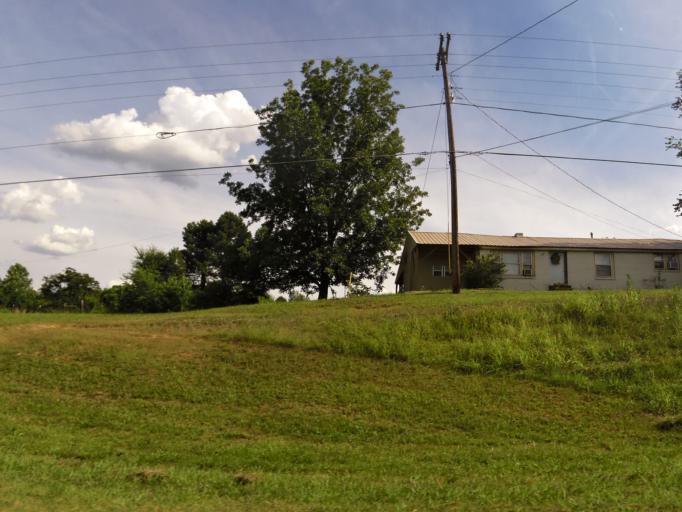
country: US
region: Tennessee
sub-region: Carroll County
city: Huntingdon
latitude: 36.0313
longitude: -88.3392
